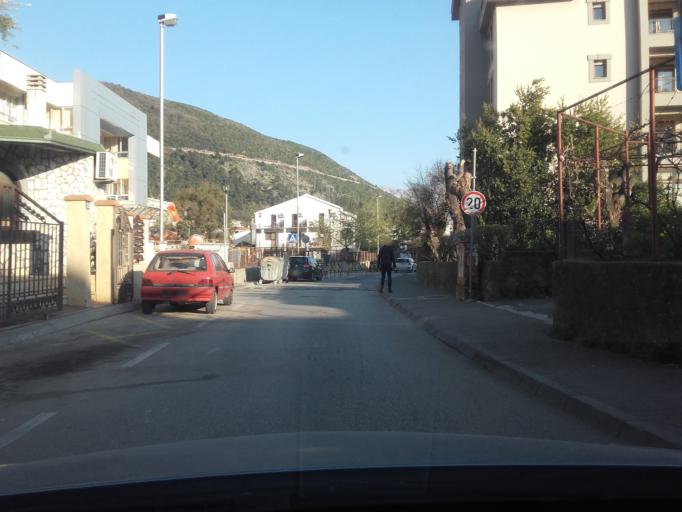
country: ME
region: Budva
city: Budva
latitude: 42.2929
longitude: 18.8447
